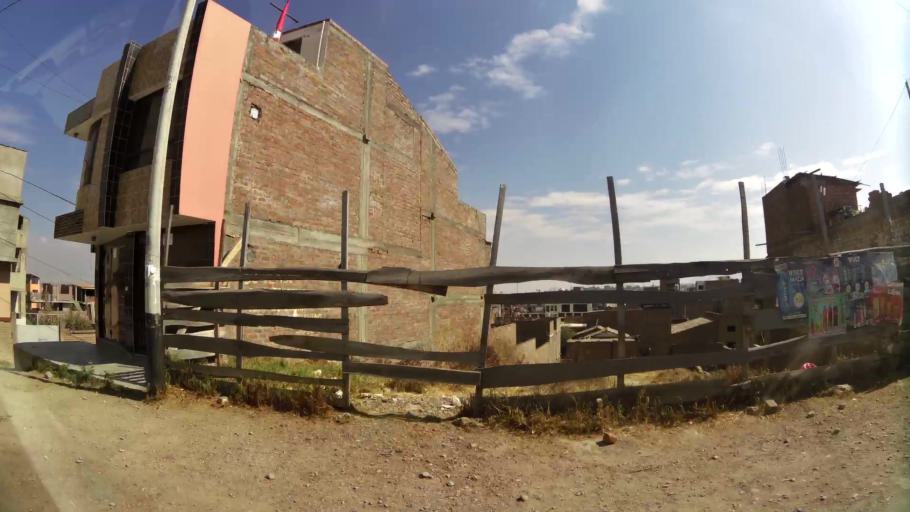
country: PE
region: Junin
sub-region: Provincia de Huancayo
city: El Tambo
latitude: -12.0769
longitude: -75.2240
